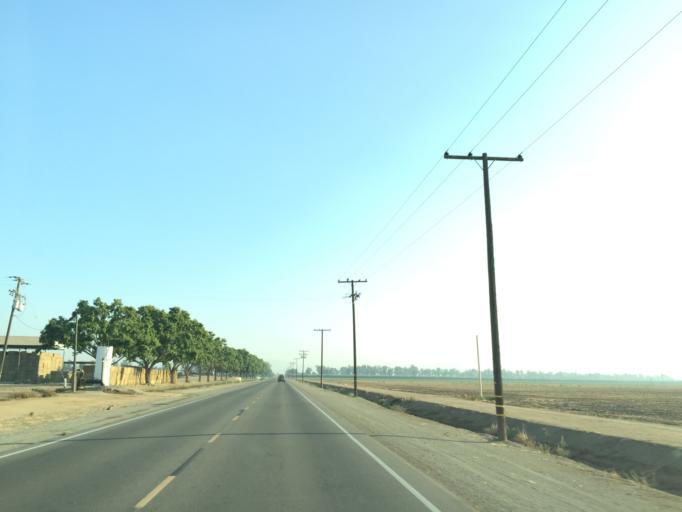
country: US
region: California
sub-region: Tulare County
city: Cutler
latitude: 36.4532
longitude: -119.2776
